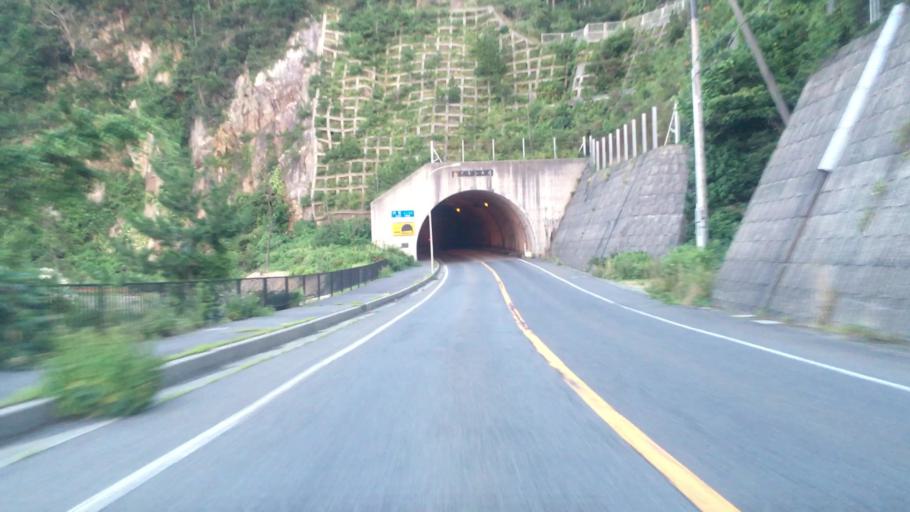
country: JP
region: Tottori
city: Tottori
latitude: 35.6161
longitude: 134.4004
